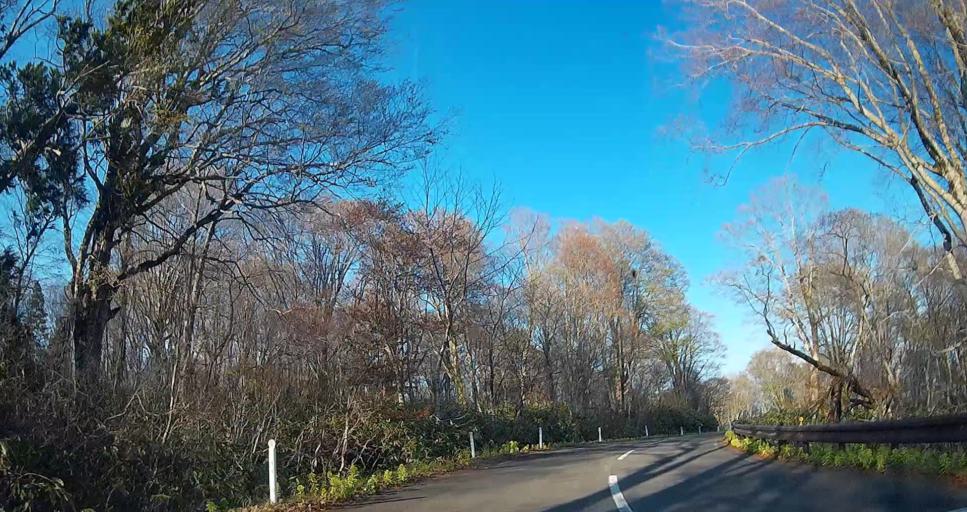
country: JP
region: Aomori
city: Mutsu
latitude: 41.3076
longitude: 141.1174
